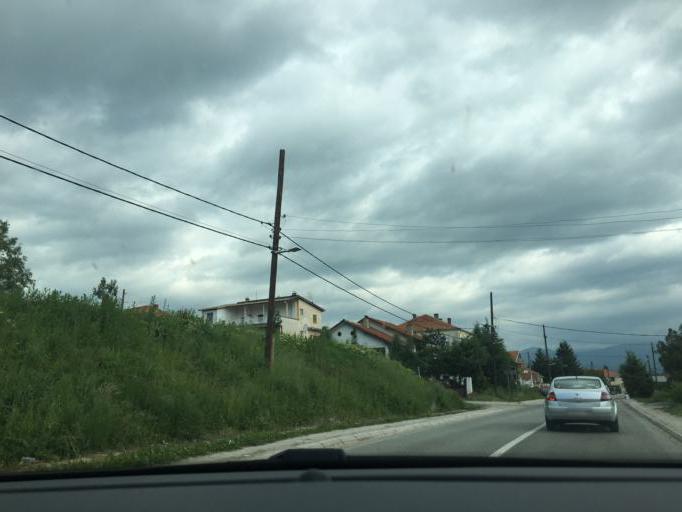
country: MK
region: Resen
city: Resen
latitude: 41.0853
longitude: 21.0085
